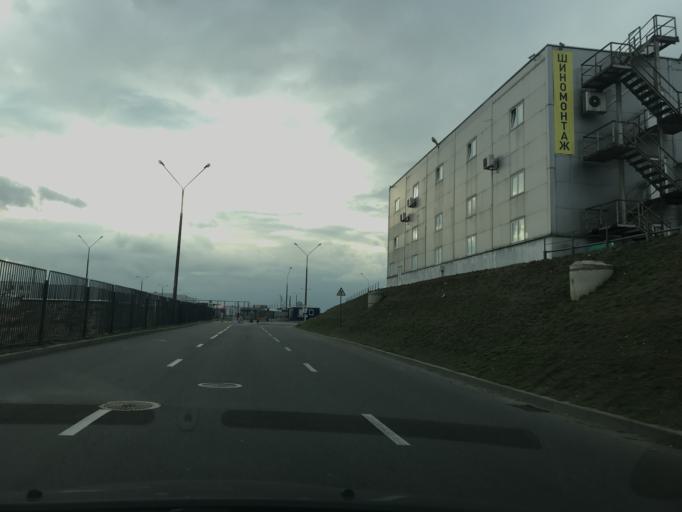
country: BY
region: Minsk
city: Borovlyany
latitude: 53.9636
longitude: 27.6301
